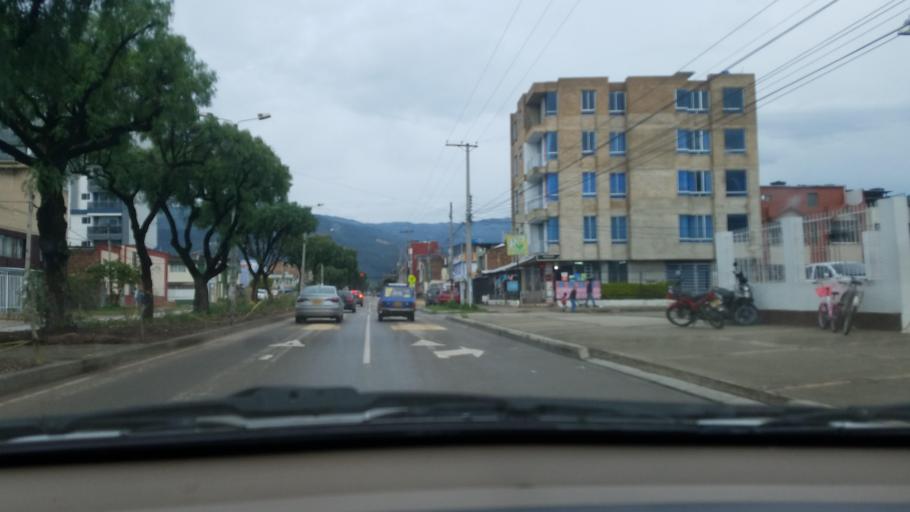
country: CO
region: Boyaca
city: Sogamoso
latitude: 5.7131
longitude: -72.9353
